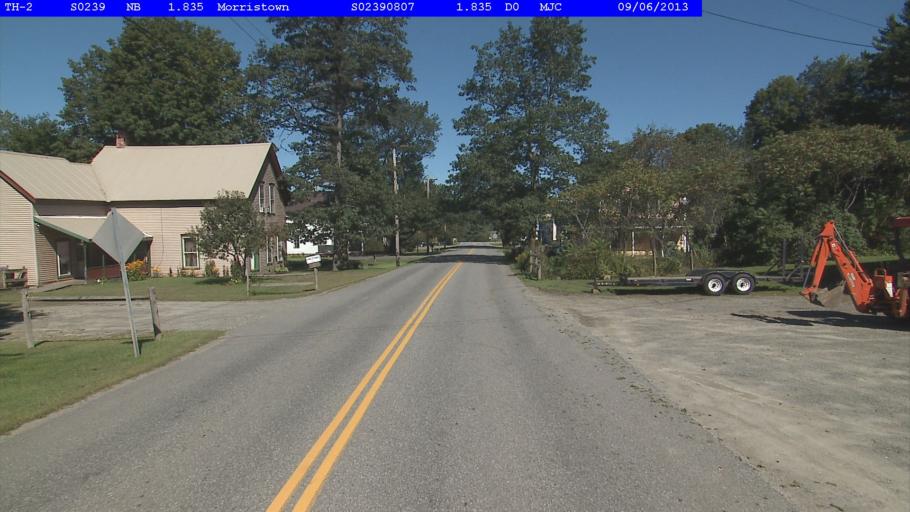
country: US
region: Vermont
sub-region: Lamoille County
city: Hyde Park
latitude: 44.5801
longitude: -72.6129
